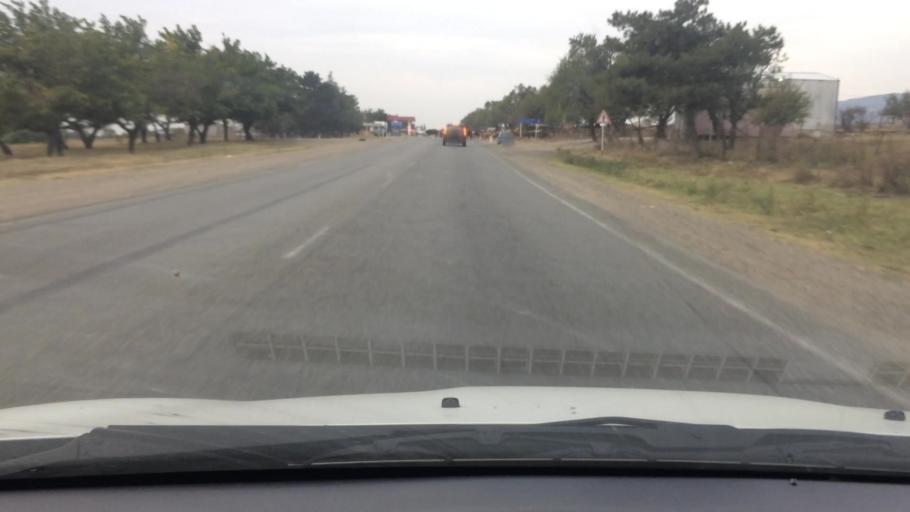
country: GE
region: T'bilisi
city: Tbilisi
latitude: 41.6356
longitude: 44.8228
